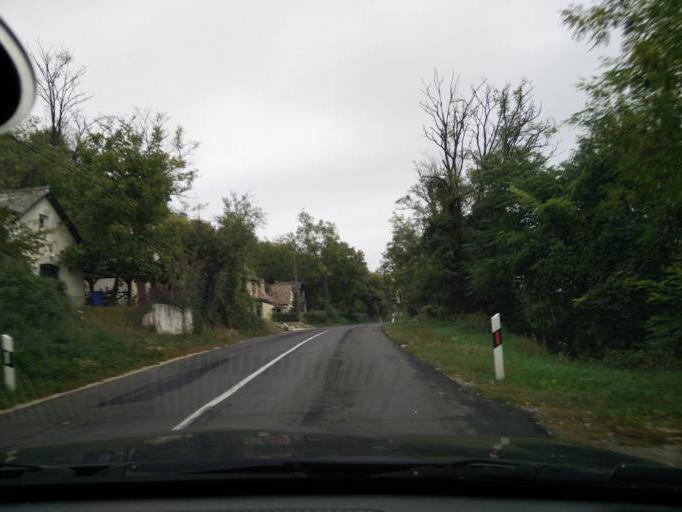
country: HU
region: Komarom-Esztergom
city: Tat
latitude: 47.7198
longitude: 18.6287
